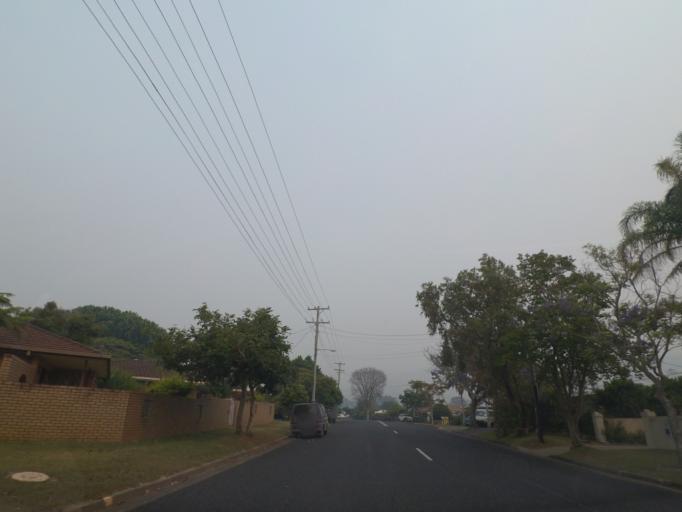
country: AU
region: New South Wales
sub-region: Coffs Harbour
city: Coffs Harbour
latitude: -30.2862
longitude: 153.1070
